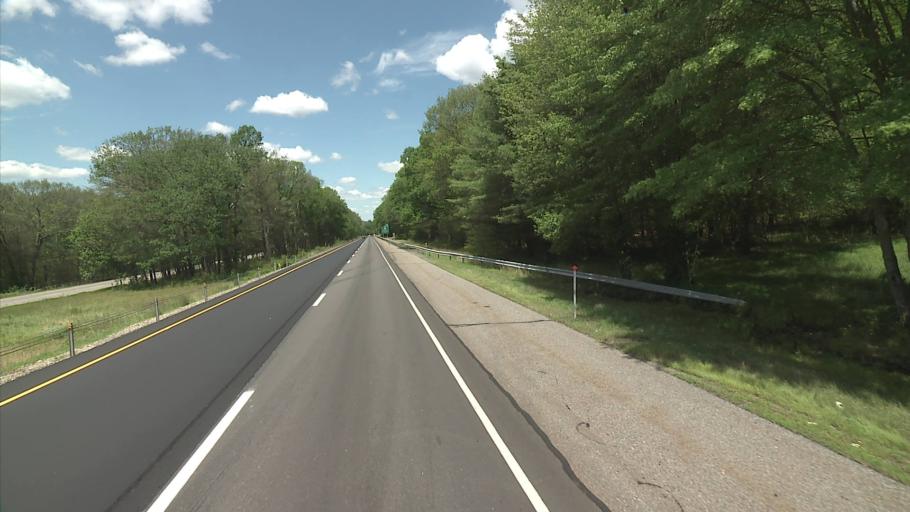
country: US
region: Connecticut
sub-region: Windham County
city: Killingly Center
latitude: 41.8233
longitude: -71.8715
